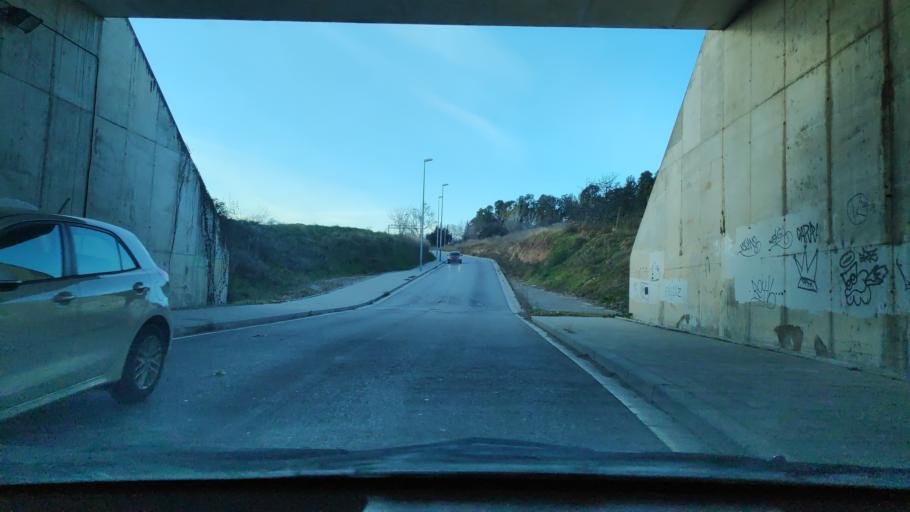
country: ES
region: Catalonia
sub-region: Provincia de Barcelona
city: Montmelo
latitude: 41.5620
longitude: 2.2563
